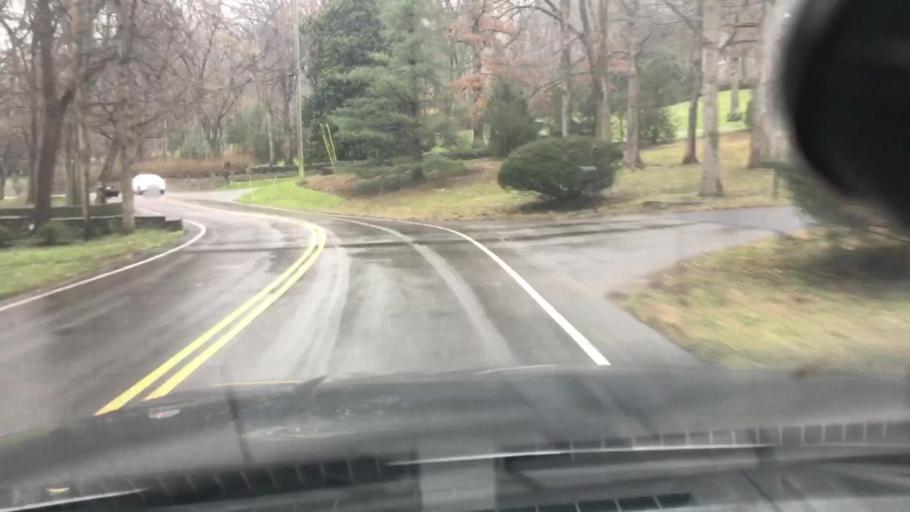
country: US
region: Tennessee
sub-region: Davidson County
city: Forest Hills
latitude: 36.0705
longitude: -86.8605
